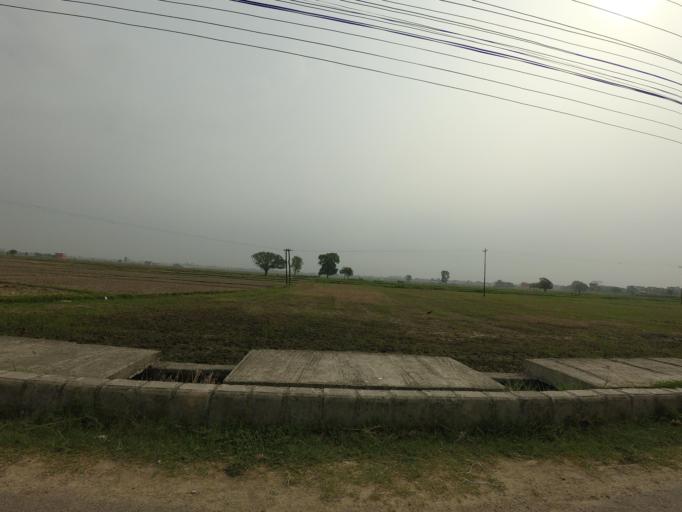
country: NP
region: Western Region
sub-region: Lumbini Zone
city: Bhairahawa
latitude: 27.4886
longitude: 83.4353
